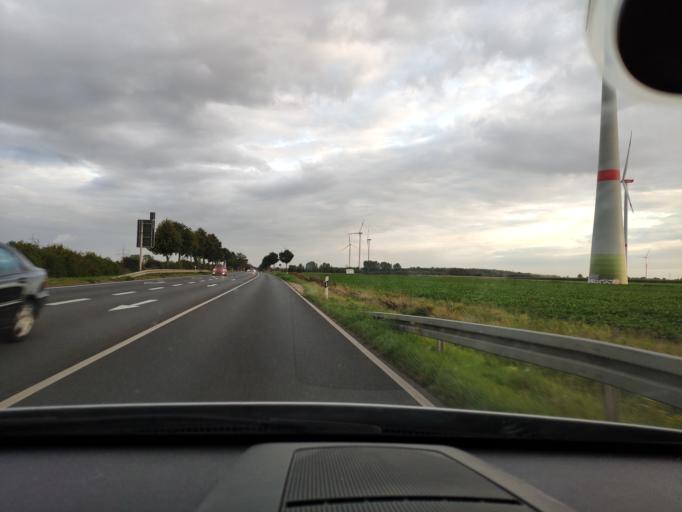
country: DE
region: North Rhine-Westphalia
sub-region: Regierungsbezirk Koln
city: Heinsberg
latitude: 51.0212
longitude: 6.1126
